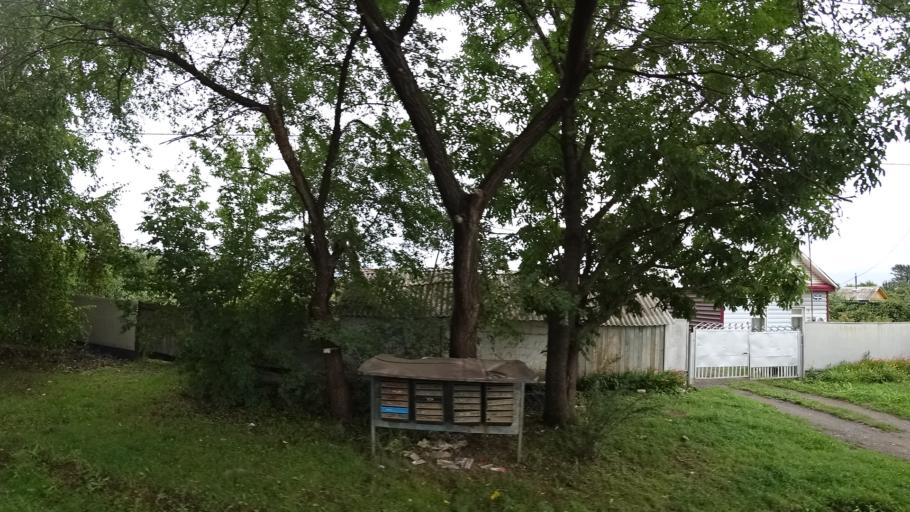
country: RU
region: Primorskiy
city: Chernigovka
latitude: 44.3346
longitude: 132.5633
